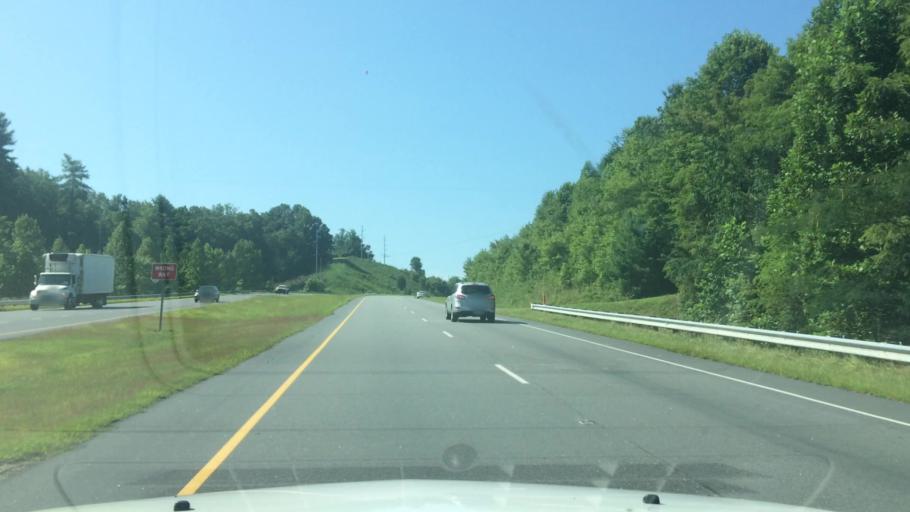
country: US
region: North Carolina
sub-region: Caldwell County
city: Lenoir
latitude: 36.0045
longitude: -81.5692
